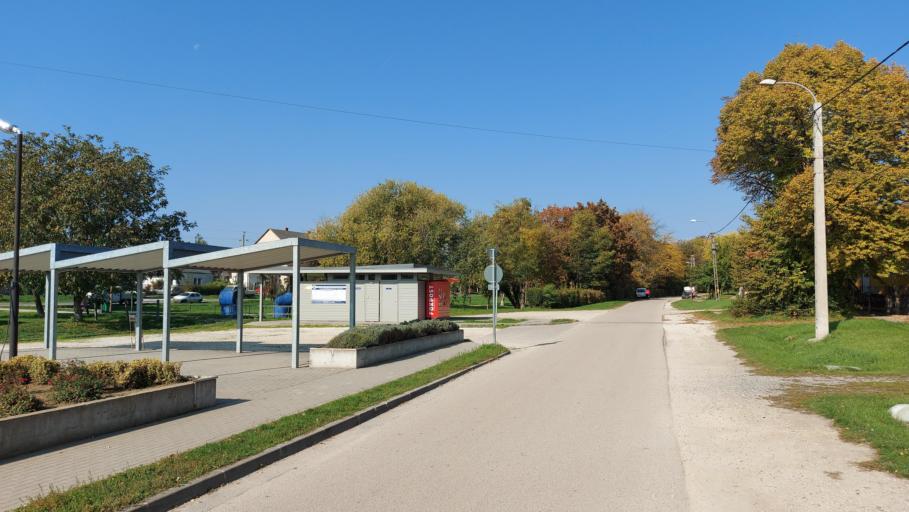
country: HU
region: Fejer
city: Polgardi
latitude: 47.0592
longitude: 18.2931
